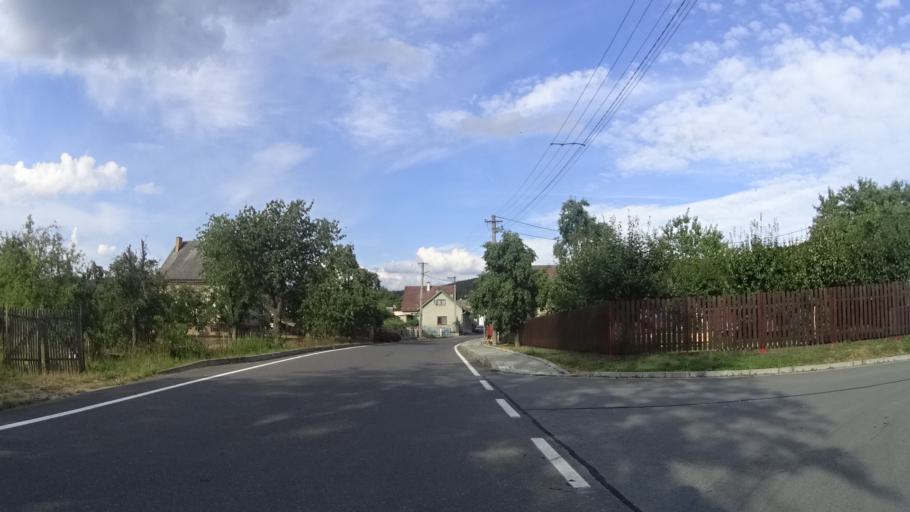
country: CZ
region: Olomoucky
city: Dubicko
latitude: 49.8437
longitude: 16.9483
